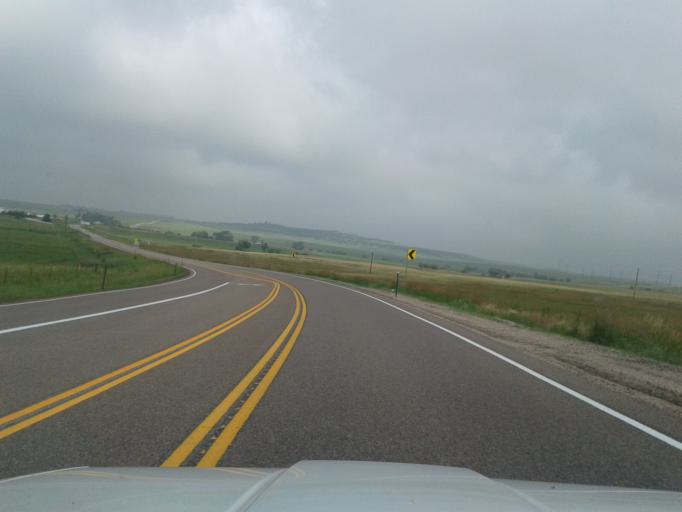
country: US
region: Colorado
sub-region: Elbert County
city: Elizabeth
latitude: 39.2613
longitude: -104.7042
